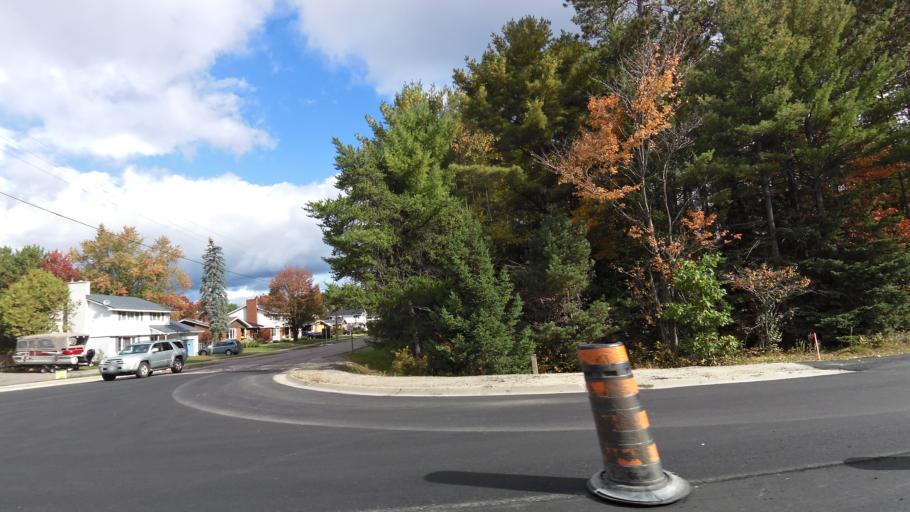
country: CA
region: Ontario
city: Deep River
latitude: 46.1020
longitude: -77.5034
